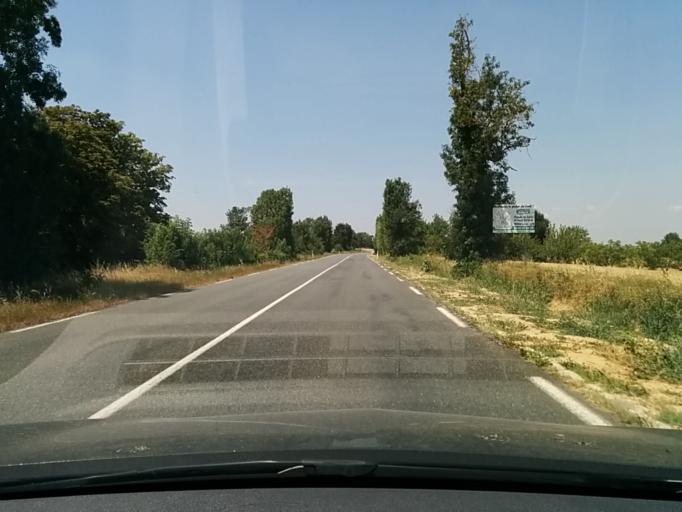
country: FR
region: Midi-Pyrenees
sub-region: Departement du Gers
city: Gimont
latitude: 43.6044
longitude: 0.9952
